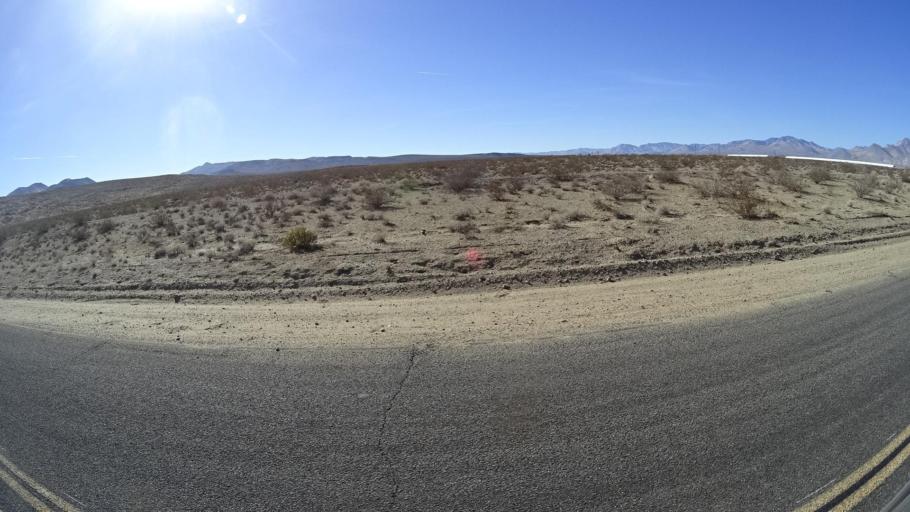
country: US
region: California
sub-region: Kern County
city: China Lake Acres
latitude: 35.5659
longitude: -117.7767
